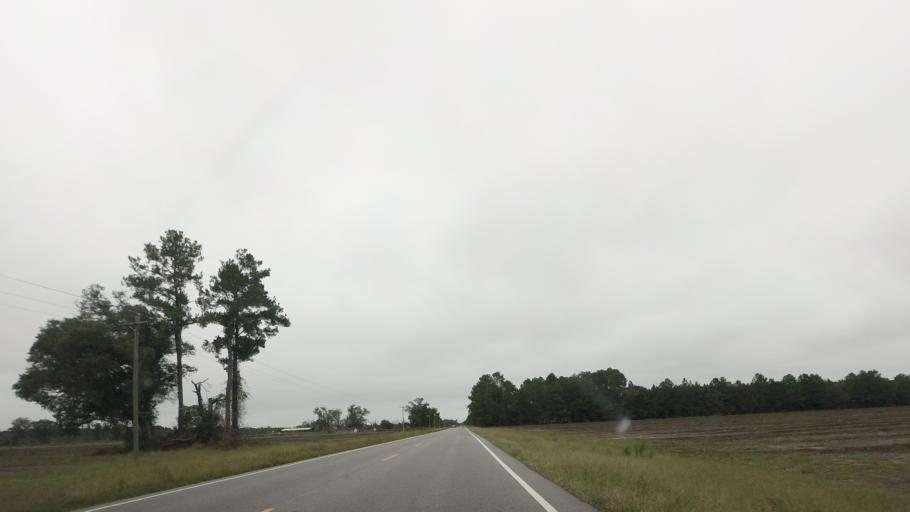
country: US
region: Georgia
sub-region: Berrien County
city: Nashville
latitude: 31.3100
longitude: -83.2322
